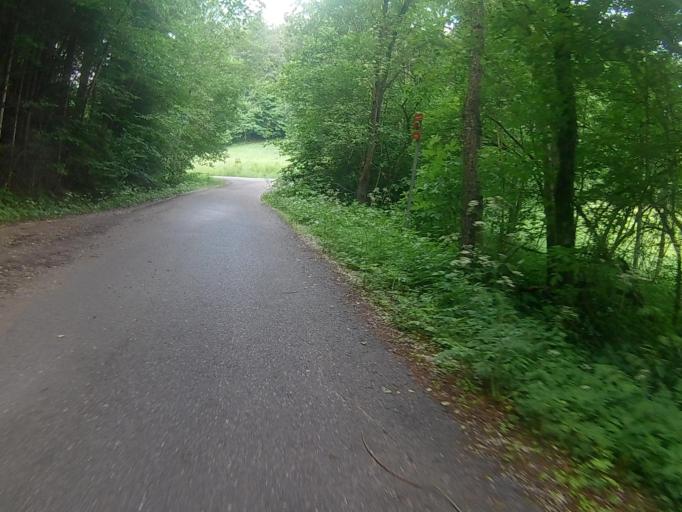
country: SI
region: Maribor
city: Kamnica
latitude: 46.6011
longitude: 15.5922
